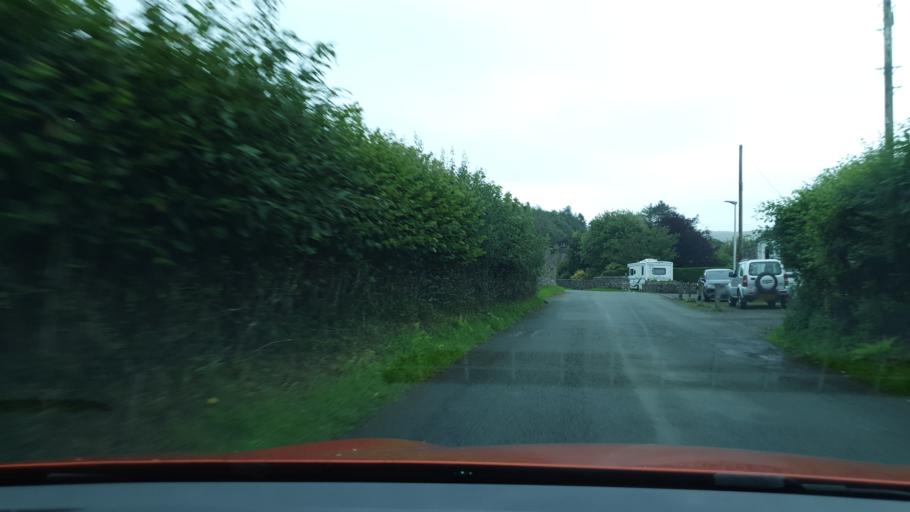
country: GB
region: England
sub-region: Cumbria
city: Seascale
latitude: 54.3903
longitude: -3.3352
